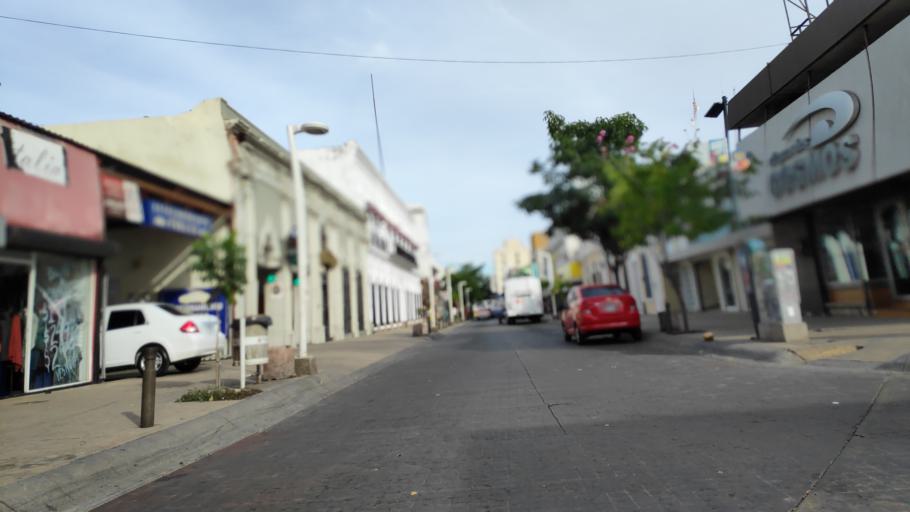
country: MX
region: Sinaloa
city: Culiacan
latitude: 24.8094
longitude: -107.3983
